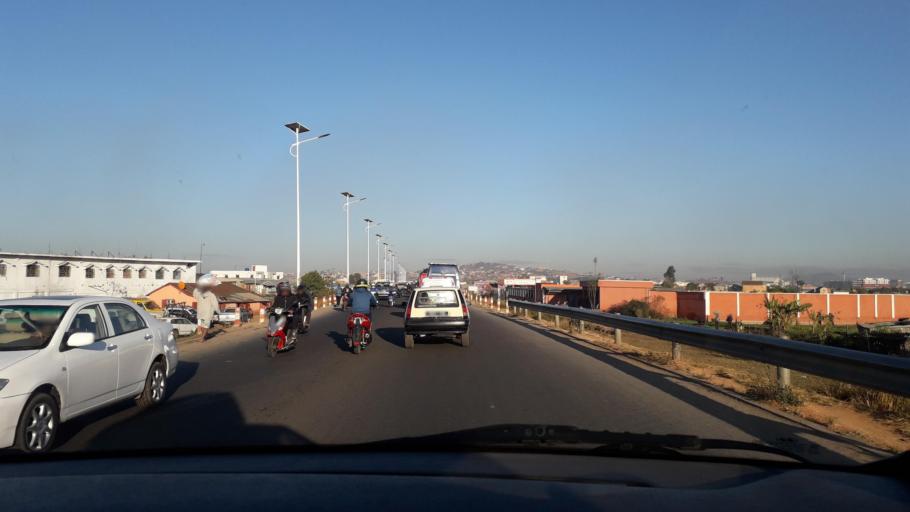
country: MG
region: Analamanga
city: Antananarivo
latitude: -18.8939
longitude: 47.5069
